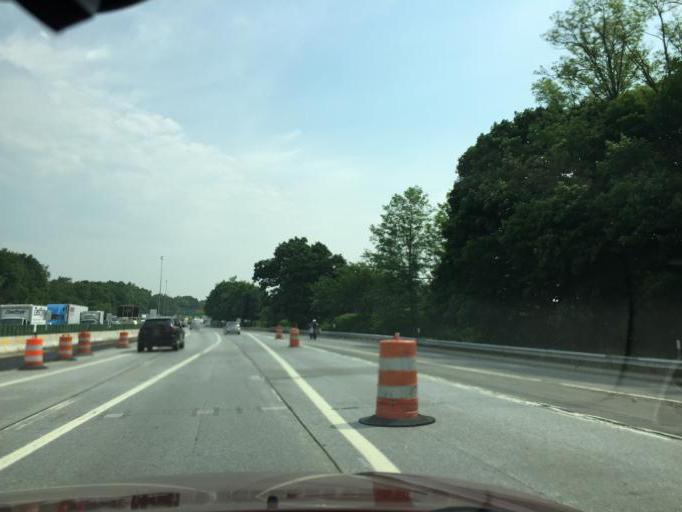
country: US
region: New York
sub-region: Westchester County
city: New Rochelle
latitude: 40.9189
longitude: -73.7789
